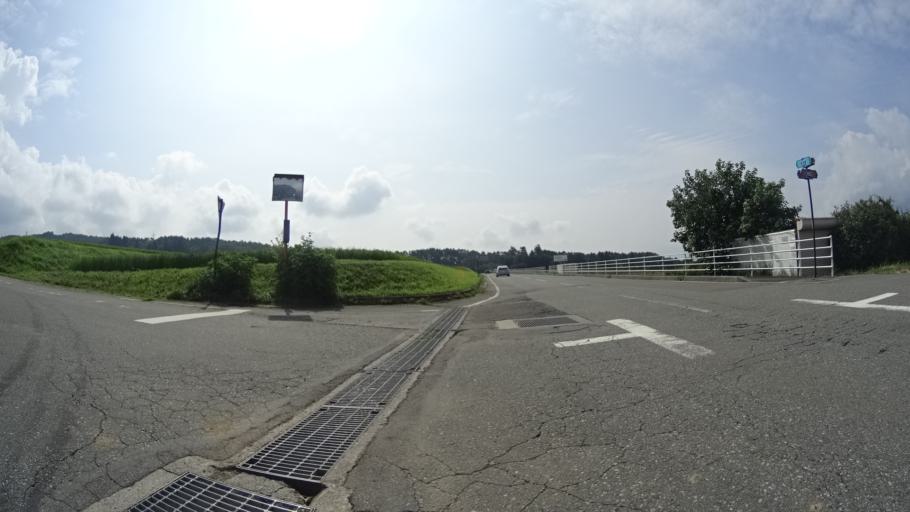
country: JP
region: Nagano
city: Chino
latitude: 35.8785
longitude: 138.2968
